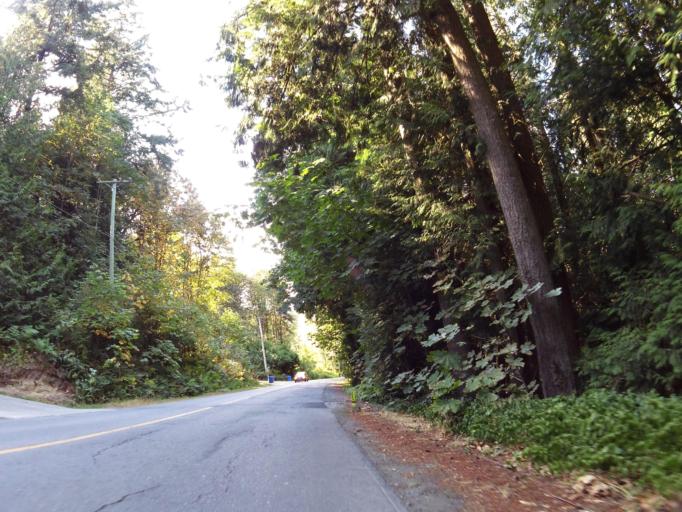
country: CA
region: British Columbia
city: North Saanich
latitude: 48.6935
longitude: -123.5646
